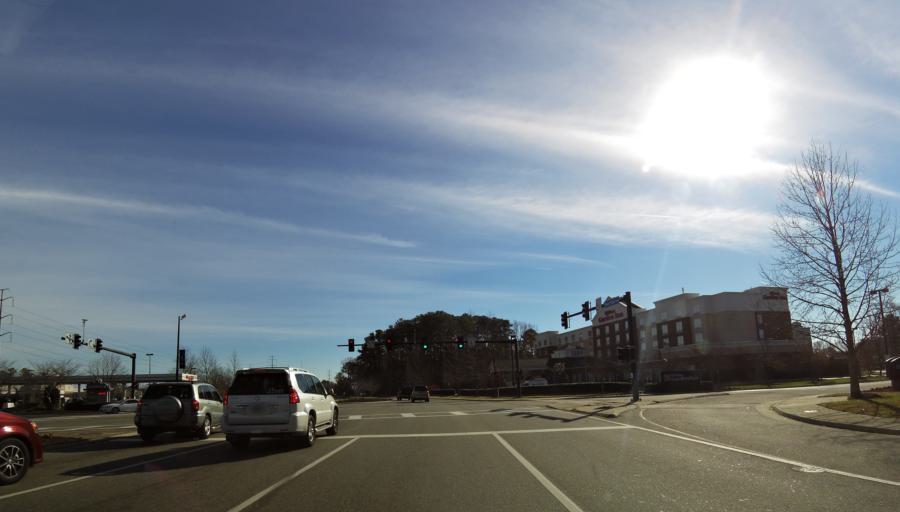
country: US
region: Virginia
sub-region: City of Hampton
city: Hampton
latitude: 37.0367
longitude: -76.3975
